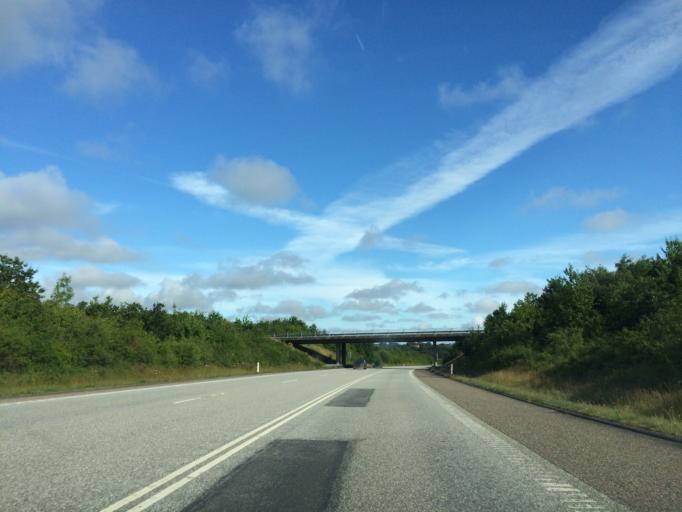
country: DK
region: Central Jutland
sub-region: Silkeborg Kommune
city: Kjellerup
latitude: 56.3390
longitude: 9.5359
